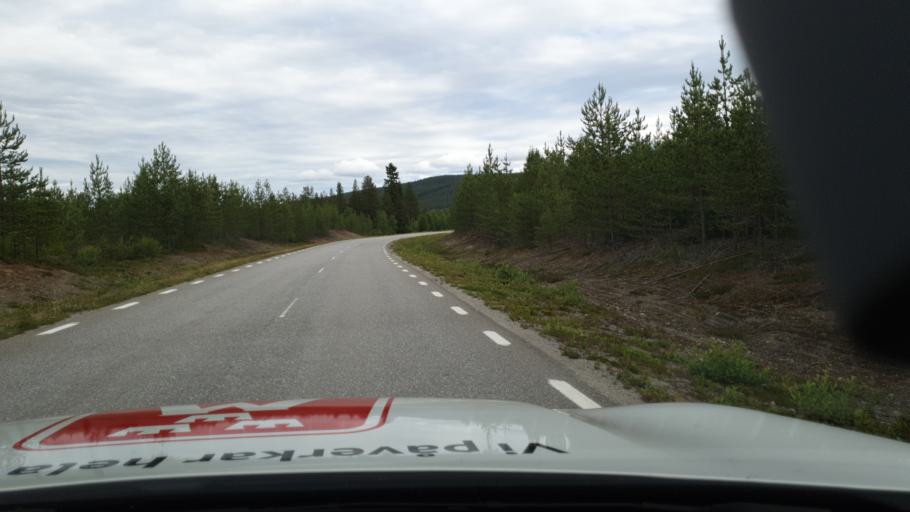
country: SE
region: Vaesterbotten
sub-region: Sorsele Kommun
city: Sorsele
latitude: 65.5386
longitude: 17.3977
